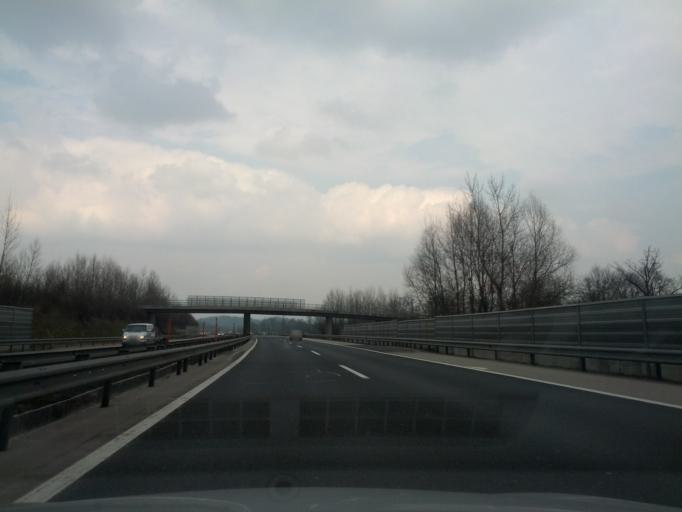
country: SI
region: Dol pri Ljubljani
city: Dol pri Ljubljani
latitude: 46.1116
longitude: 14.6013
